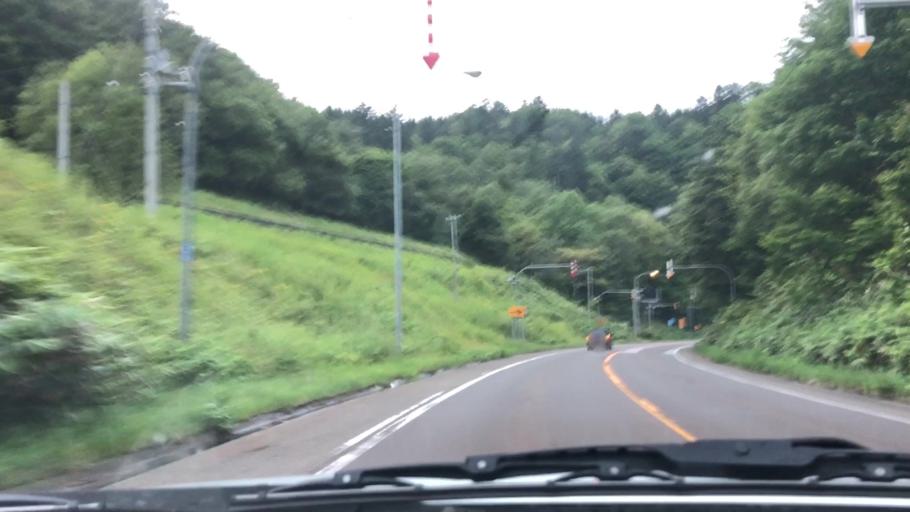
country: JP
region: Hokkaido
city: Iwamizawa
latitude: 42.9198
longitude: 142.1164
